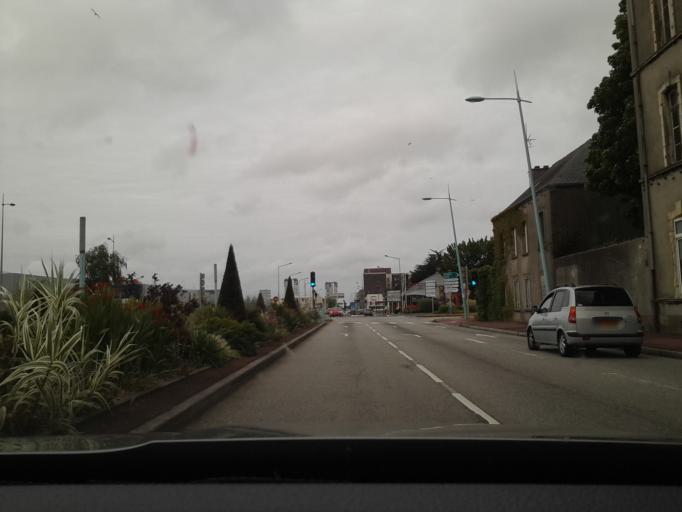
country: FR
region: Lower Normandy
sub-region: Departement de la Manche
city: Cherbourg-Octeville
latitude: 49.6328
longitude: -1.6175
